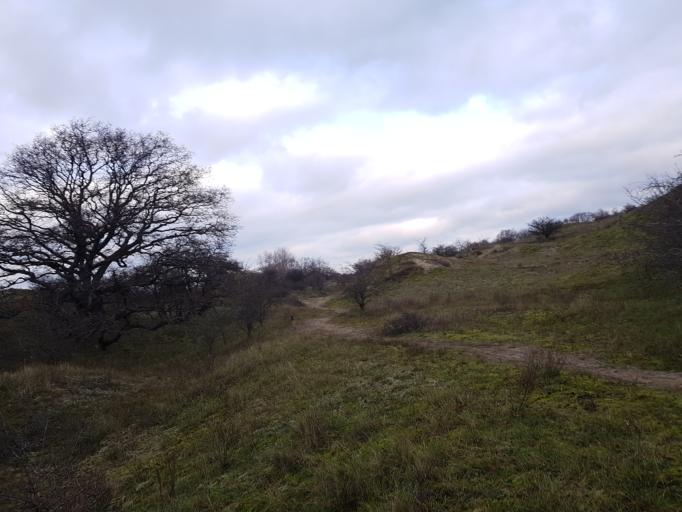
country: NL
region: South Holland
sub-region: Gemeente Wassenaar
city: Wassenaar
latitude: 52.1514
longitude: 4.3722
